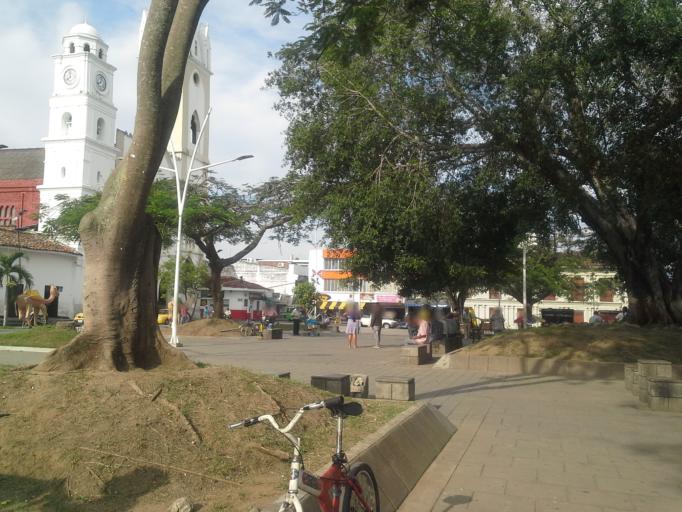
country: CO
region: Valle del Cauca
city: Tulua
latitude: 4.0854
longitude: -76.1971
